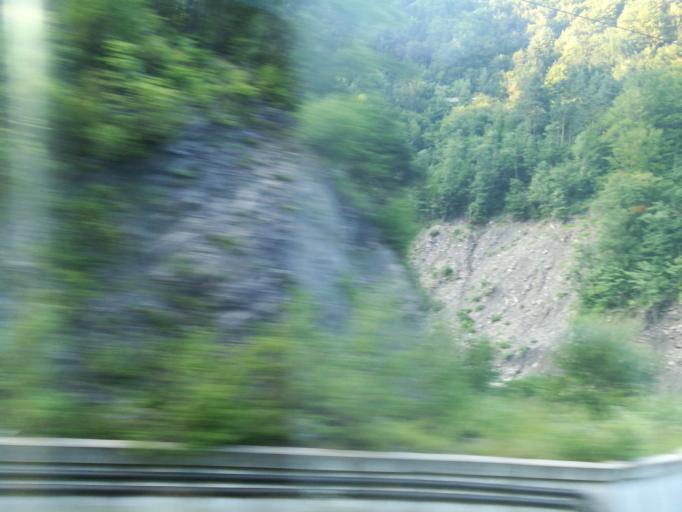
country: RO
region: Prahova
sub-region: Comuna Comarnic
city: Posada
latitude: 45.2923
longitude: 25.6001
